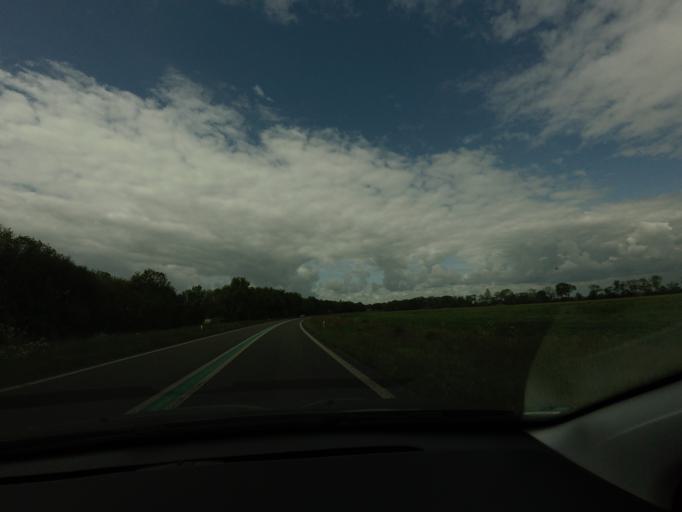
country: NL
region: Friesland
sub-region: Sudwest Fryslan
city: Koudum
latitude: 52.9065
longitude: 5.4556
